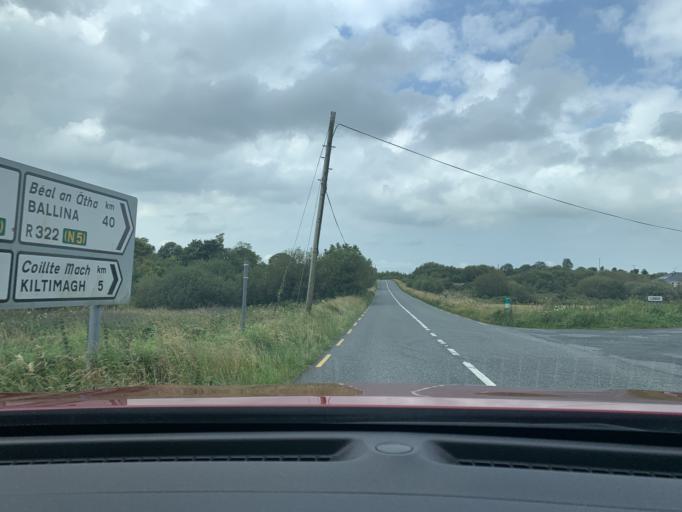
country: IE
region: Connaught
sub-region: Maigh Eo
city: Kiltamagh
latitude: 53.8559
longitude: -8.9184
